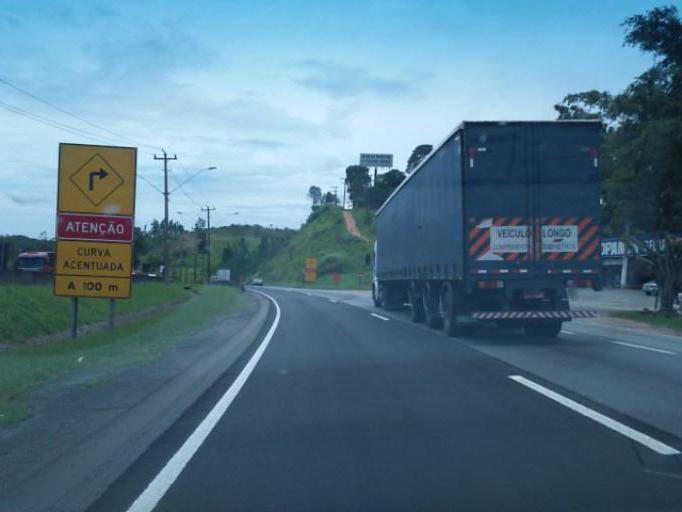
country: BR
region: Sao Paulo
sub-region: Sao Lourenco Da Serra
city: Sao Lourenco da Serra
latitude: -23.8394
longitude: -46.9314
